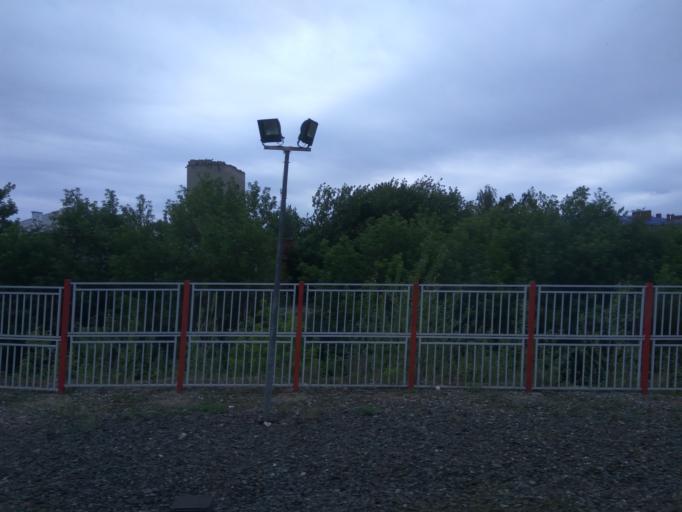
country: RU
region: Tatarstan
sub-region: Gorod Kazan'
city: Kazan
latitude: 55.8420
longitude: 49.0679
